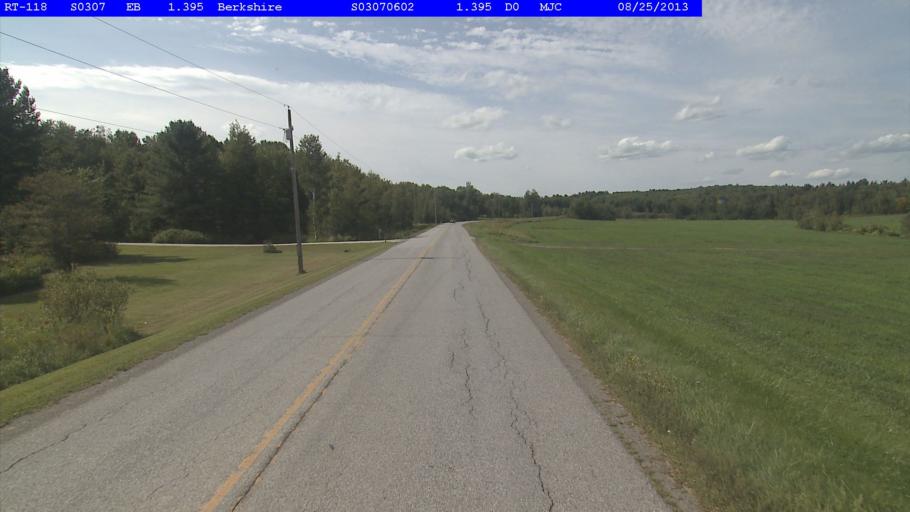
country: US
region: Vermont
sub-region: Franklin County
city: Enosburg Falls
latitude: 44.9408
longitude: -72.7367
